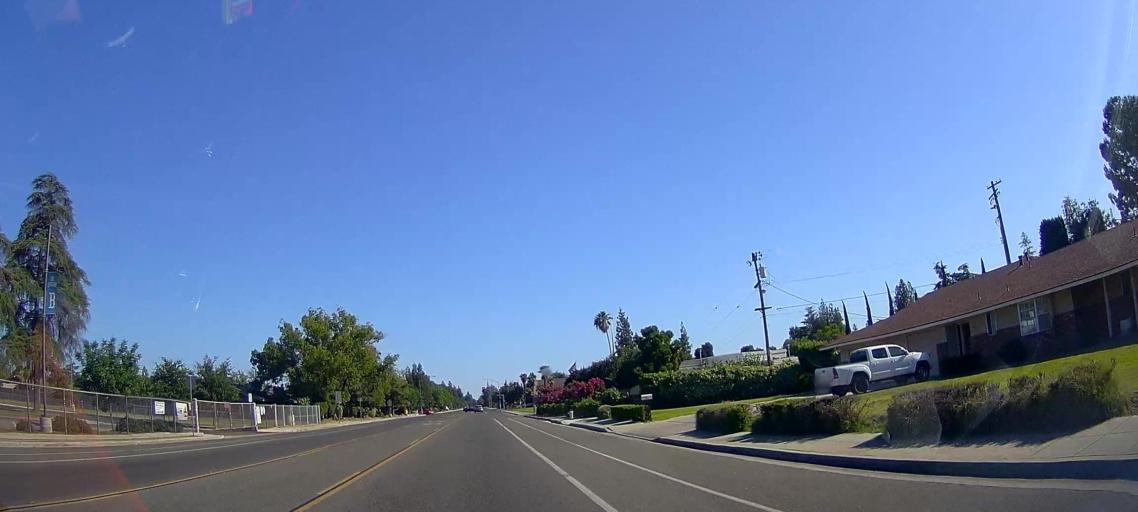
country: US
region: California
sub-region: Fresno County
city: Fresno
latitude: 36.8173
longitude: -119.7994
